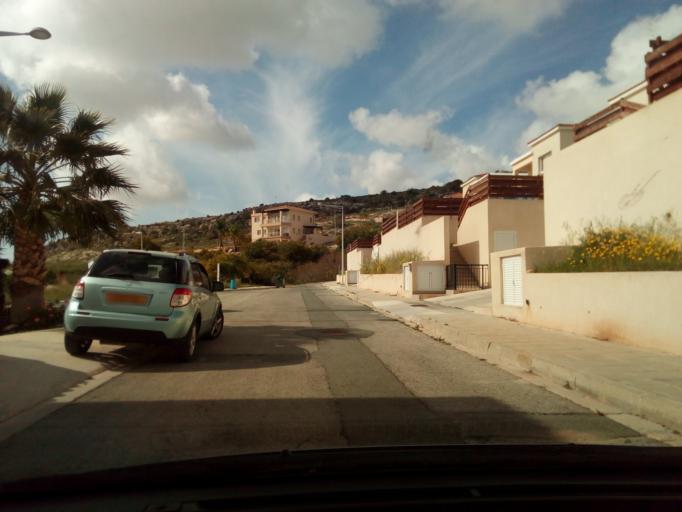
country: CY
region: Pafos
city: Paphos
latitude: 34.7668
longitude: 32.4663
